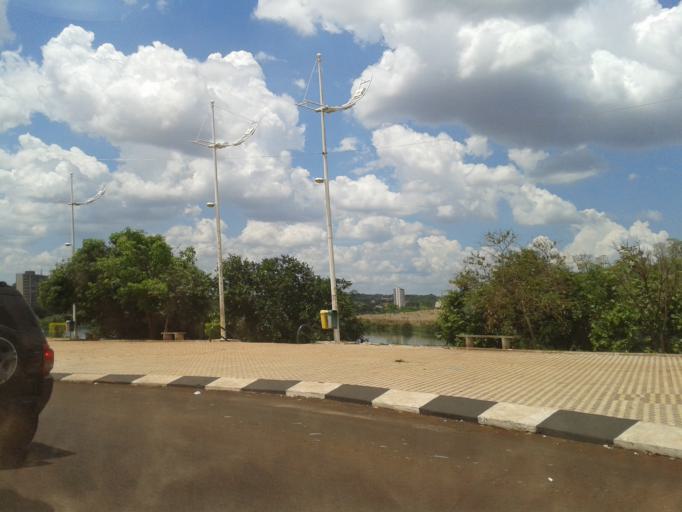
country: BR
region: Goias
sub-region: Itumbiara
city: Itumbiara
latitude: -18.4191
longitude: -49.2139
